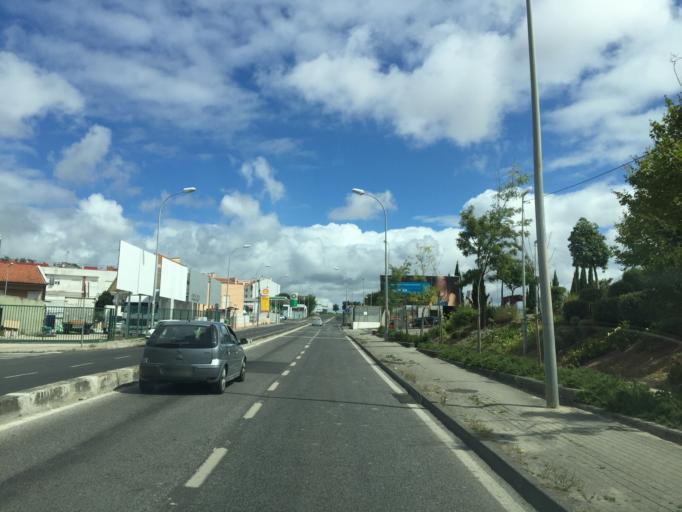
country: PT
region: Lisbon
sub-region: Amadora
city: Amadora
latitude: 38.7755
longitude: -9.2303
